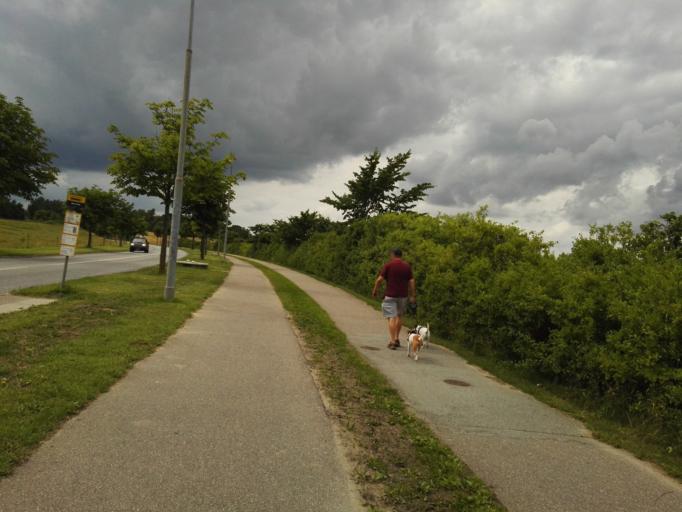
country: DK
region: Capital Region
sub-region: Egedal Kommune
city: Olstykke
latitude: 55.7892
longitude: 12.1679
